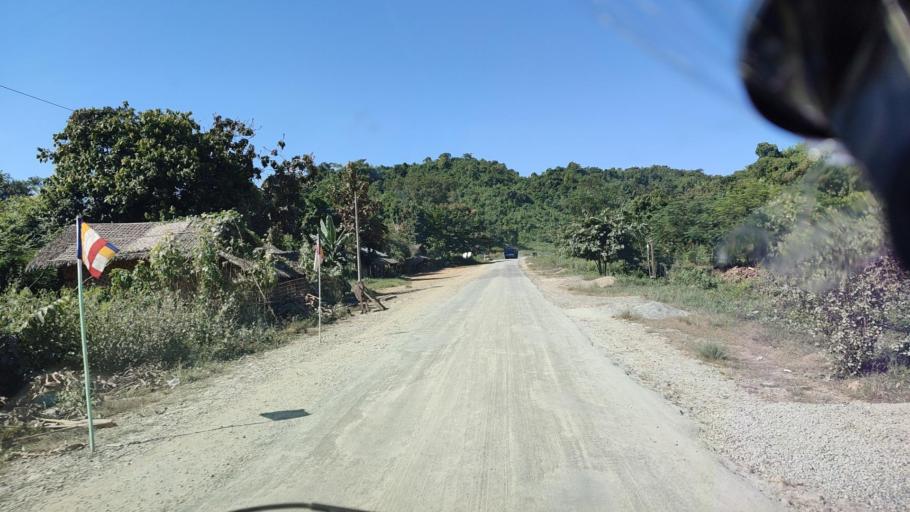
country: MM
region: Rakhine
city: Sittwe
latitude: 19.9481
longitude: 93.6614
